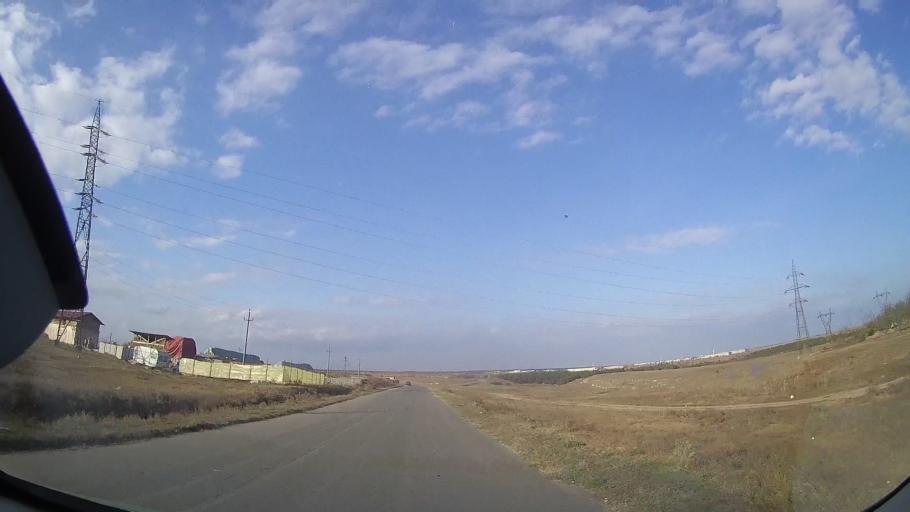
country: RO
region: Constanta
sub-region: Comuna Limanu
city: Limanu
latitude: 43.8026
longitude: 28.5217
